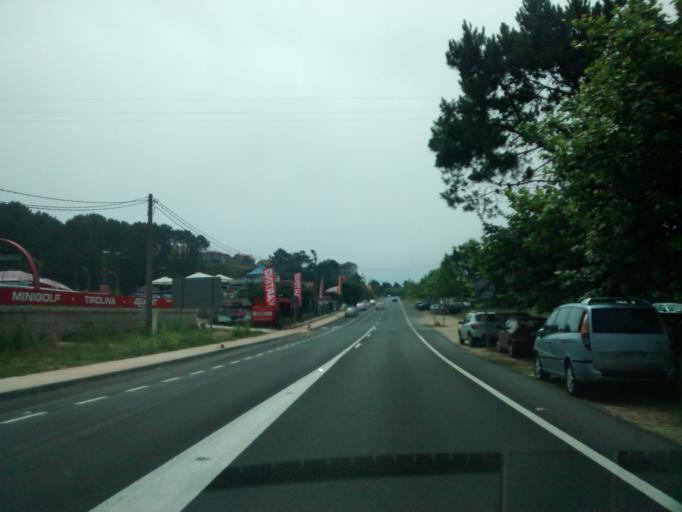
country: ES
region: Galicia
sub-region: Provincia de Pontevedra
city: Sanxenxo
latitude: 42.4160
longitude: -8.8677
